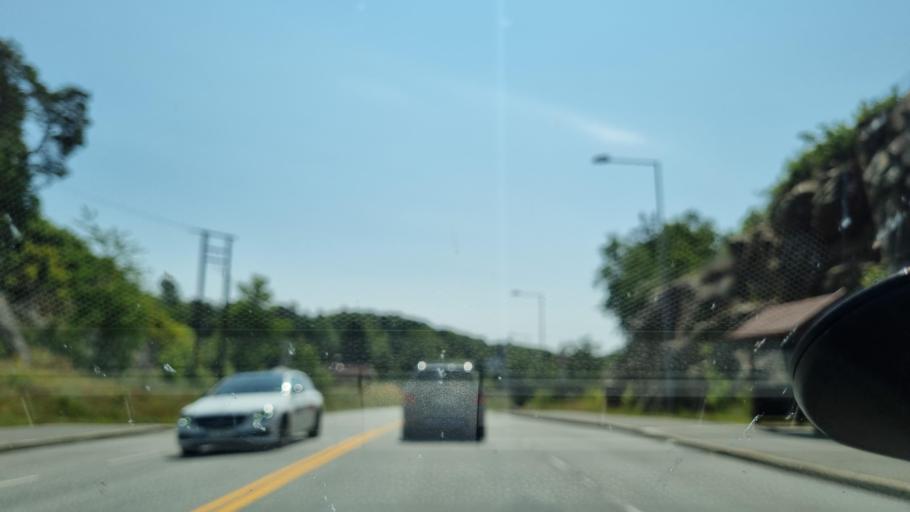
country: NO
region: Aust-Agder
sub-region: Arendal
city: Arendal
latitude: 58.4591
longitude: 8.8191
